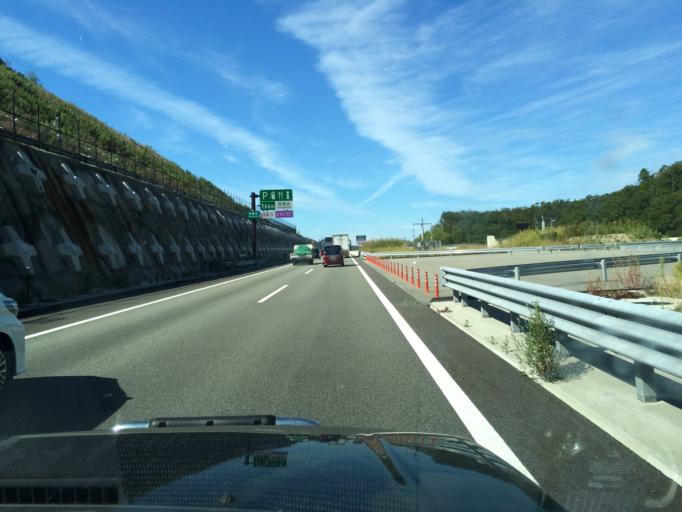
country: JP
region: Hyogo
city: Takarazuka
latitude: 34.8832
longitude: 135.3407
